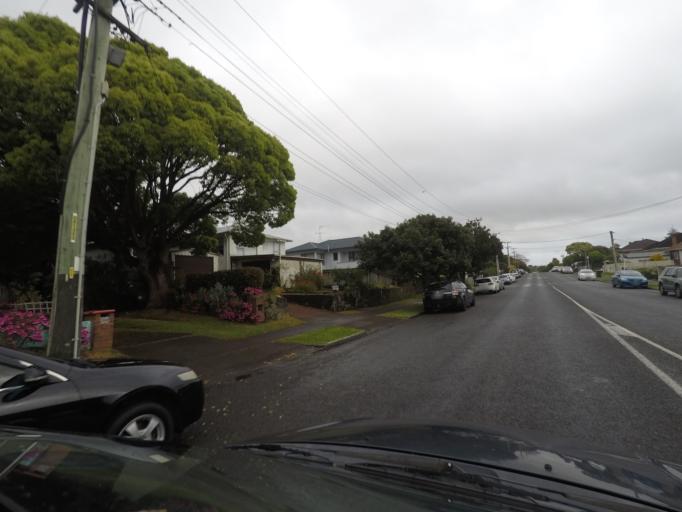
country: NZ
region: Auckland
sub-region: Auckland
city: Auckland
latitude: -36.8845
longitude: 174.7337
